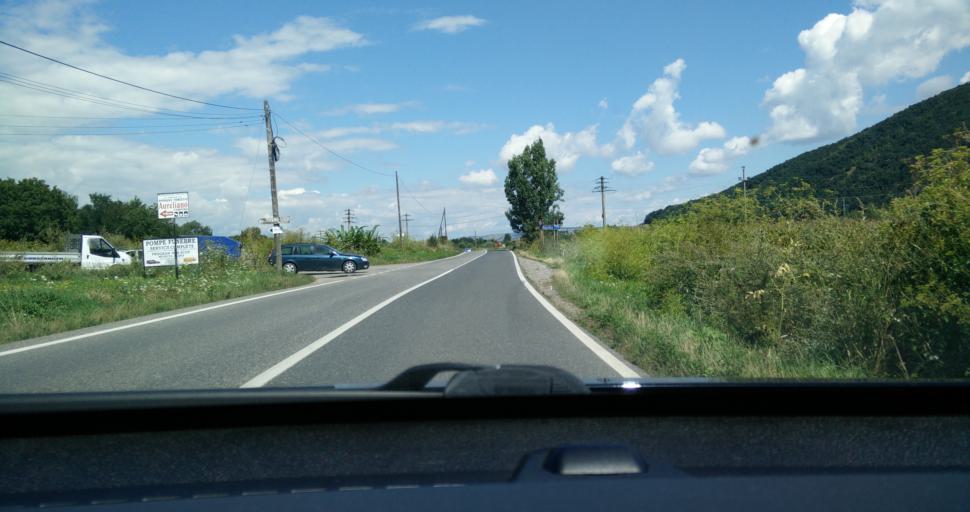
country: RO
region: Alba
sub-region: Comuna Sasciori
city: Sebesel
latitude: 45.8954
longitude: 23.5598
